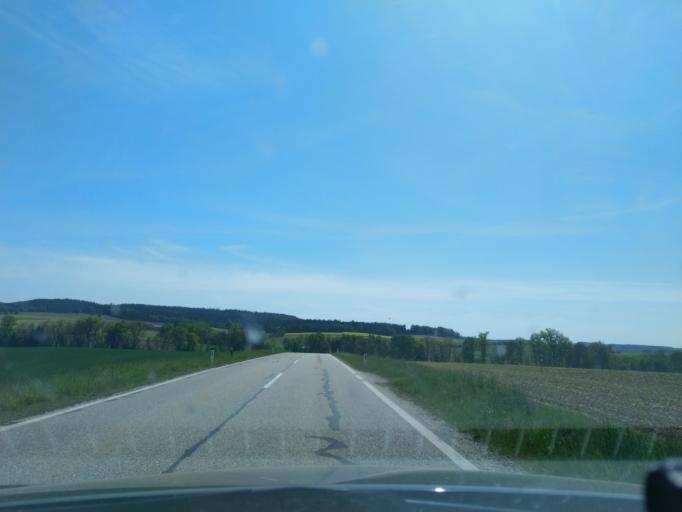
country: DE
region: Bavaria
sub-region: Lower Bavaria
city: Bad Fussing
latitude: 48.2746
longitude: 13.3551
